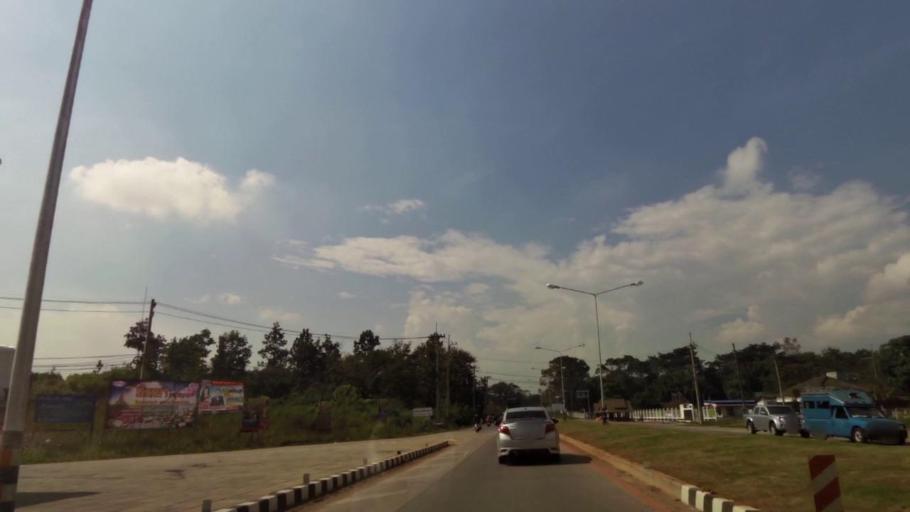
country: TH
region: Chiang Rai
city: Chiang Rai
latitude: 19.8757
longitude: 99.7856
